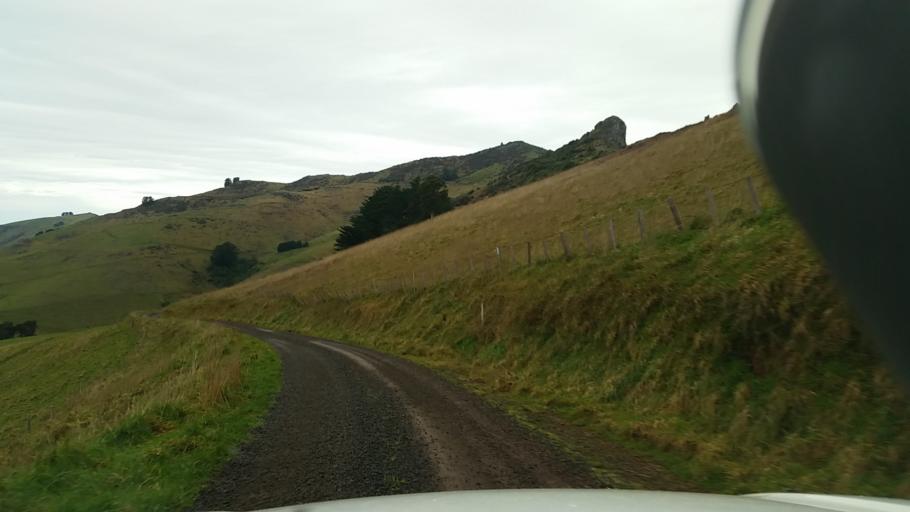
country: NZ
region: Canterbury
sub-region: Christchurch City
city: Christchurch
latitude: -43.7442
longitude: 172.9935
